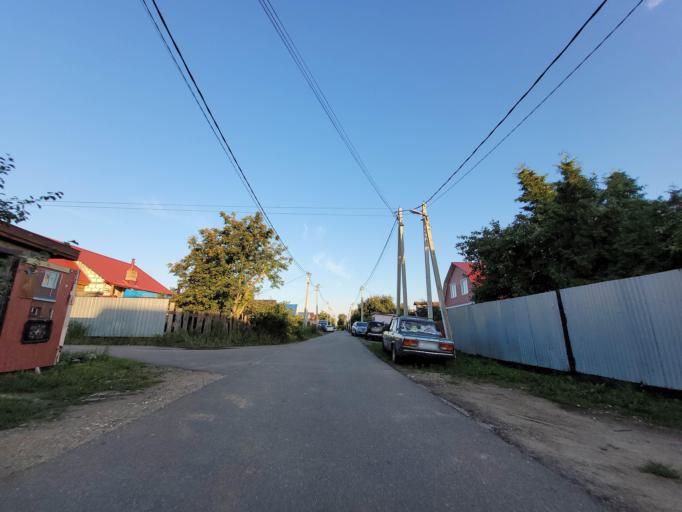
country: RU
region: Moskovskaya
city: Beloozerskiy
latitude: 55.4355
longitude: 38.4838
